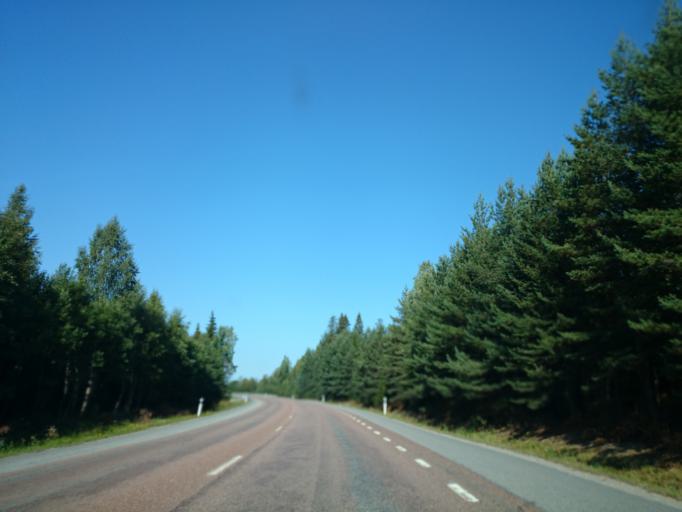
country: SE
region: Gaevleborg
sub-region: Hudiksvalls Kommun
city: Sorforsa
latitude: 61.7224
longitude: 17.0120
